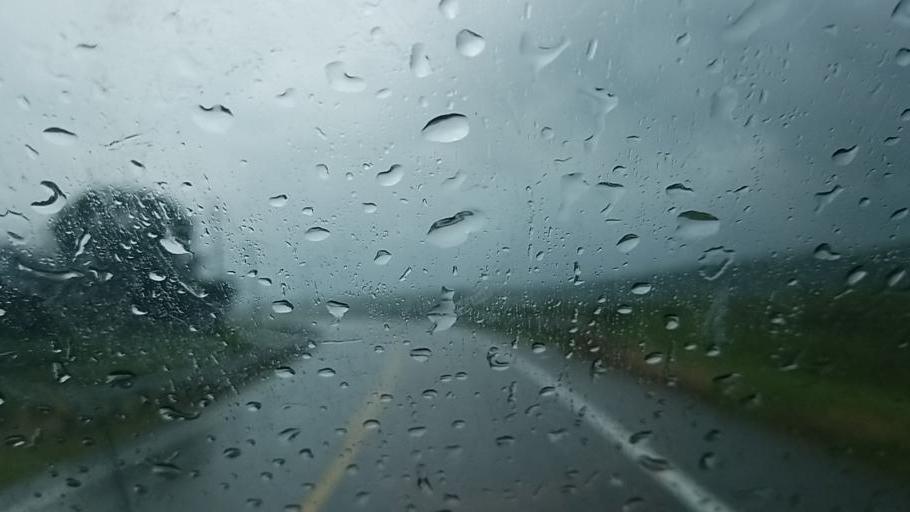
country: US
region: Ohio
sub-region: Logan County
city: Bellefontaine
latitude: 40.3255
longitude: -83.6540
